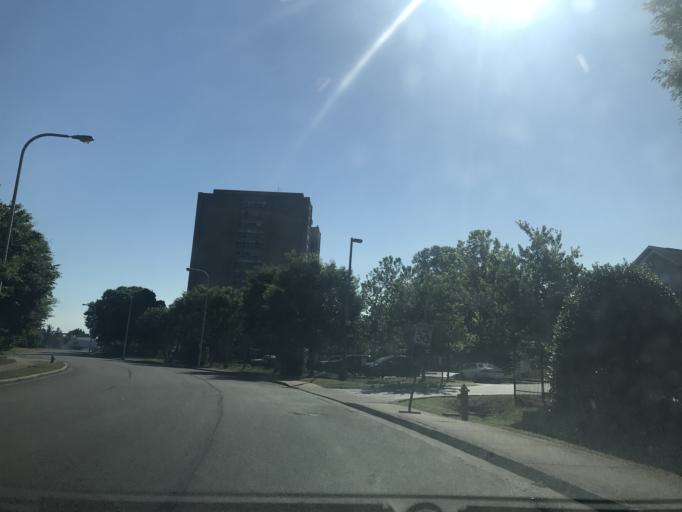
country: US
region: Tennessee
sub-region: Davidson County
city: Nashville
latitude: 36.1907
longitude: -86.8056
